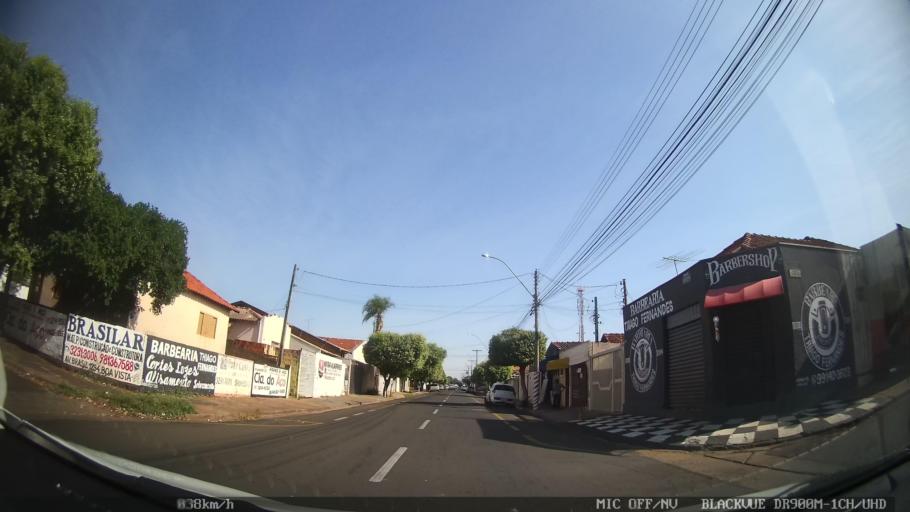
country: BR
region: Sao Paulo
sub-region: Sao Jose Do Rio Preto
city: Sao Jose do Rio Preto
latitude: -20.7956
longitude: -49.3844
